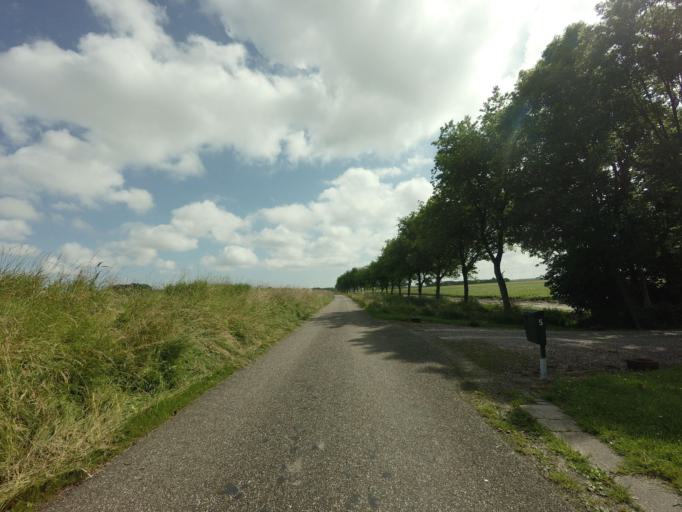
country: NL
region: North Holland
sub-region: Gemeente Schagen
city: Schagen
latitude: 52.8508
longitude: 4.8145
